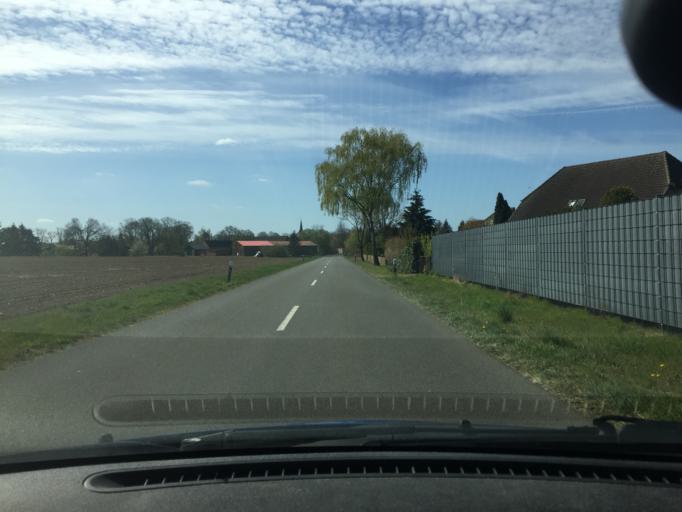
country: DE
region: Lower Saxony
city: Wieren
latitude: 52.9328
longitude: 10.6453
